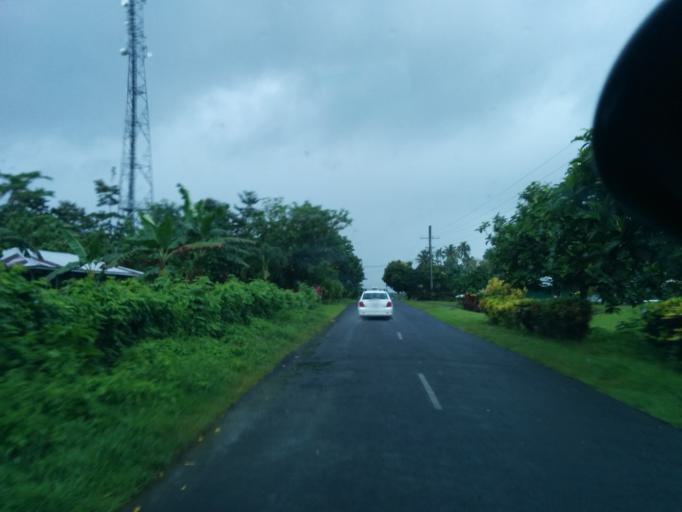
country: WS
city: Matavai
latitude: -14.0233
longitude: -171.6808
